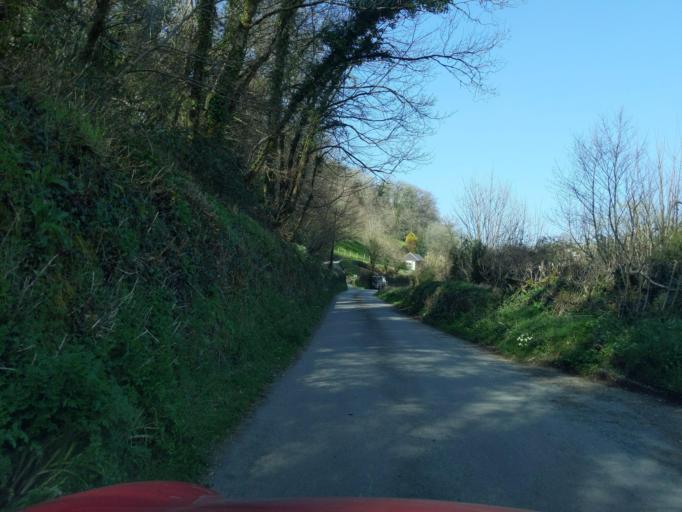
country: GB
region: England
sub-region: Devon
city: Horrabridge
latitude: 50.4699
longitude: -4.1330
